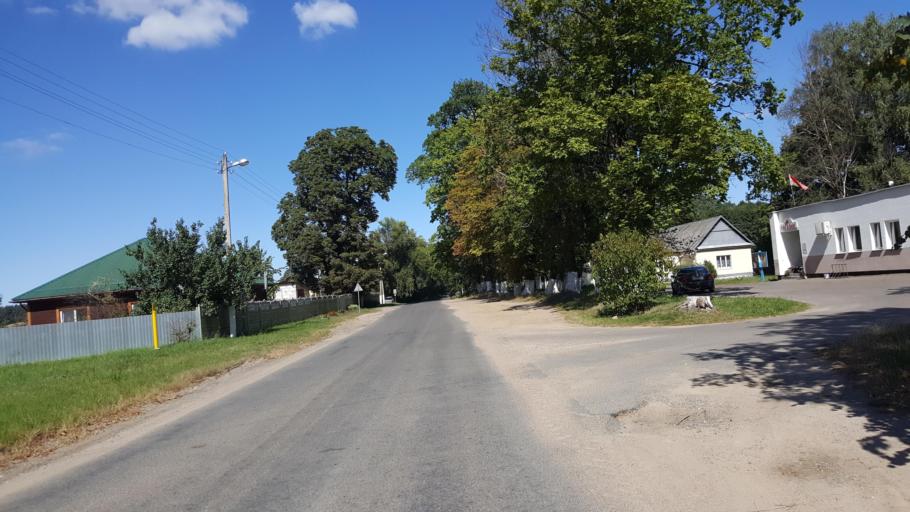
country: BY
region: Brest
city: Vysokaye
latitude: 52.2600
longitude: 23.4197
